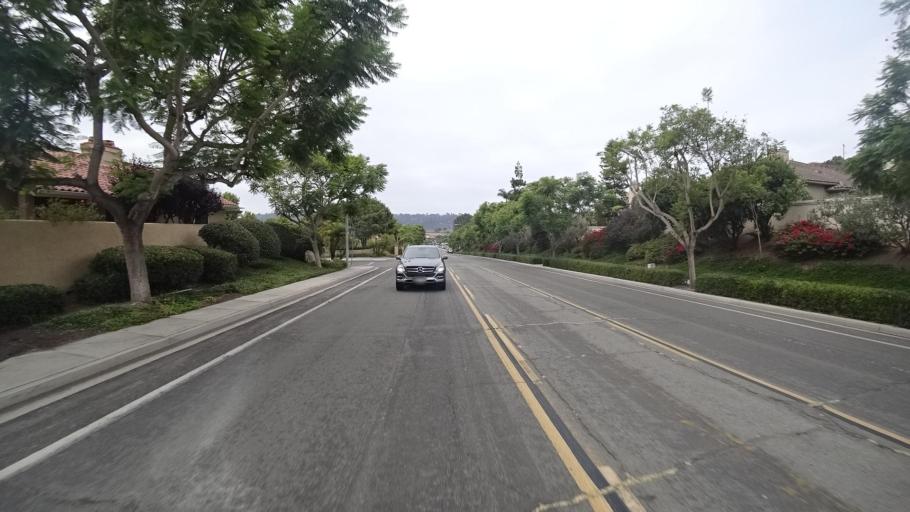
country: US
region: California
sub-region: San Diego County
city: Solana Beach
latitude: 32.9838
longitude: -117.2469
